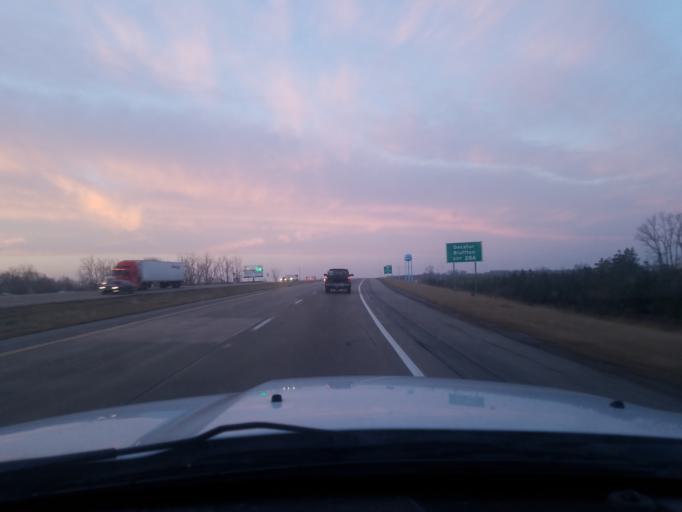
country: US
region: Indiana
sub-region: Huntington County
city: Markle
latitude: 40.8346
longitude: -85.3469
